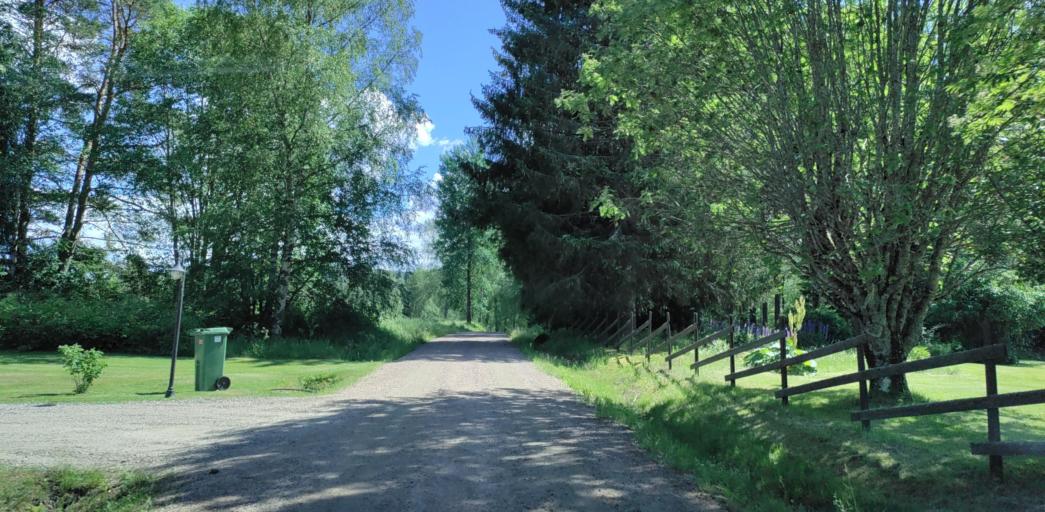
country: SE
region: Vaermland
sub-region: Munkfors Kommun
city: Munkfors
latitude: 59.9509
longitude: 13.4947
